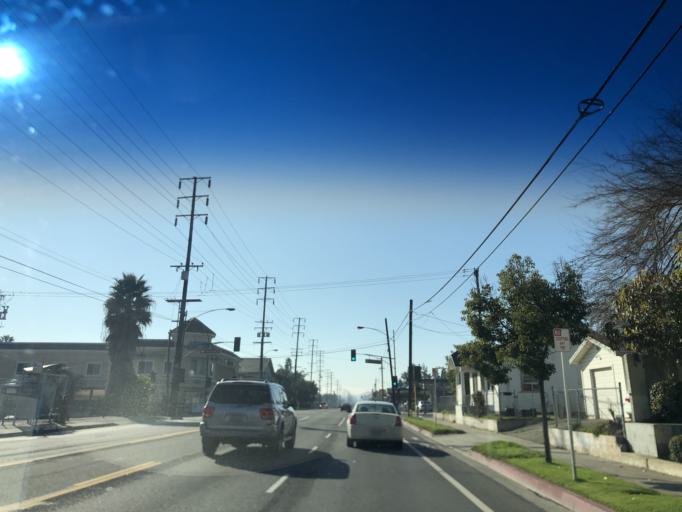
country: US
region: California
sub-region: Los Angeles County
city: South San Gabriel
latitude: 34.0760
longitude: -118.0997
